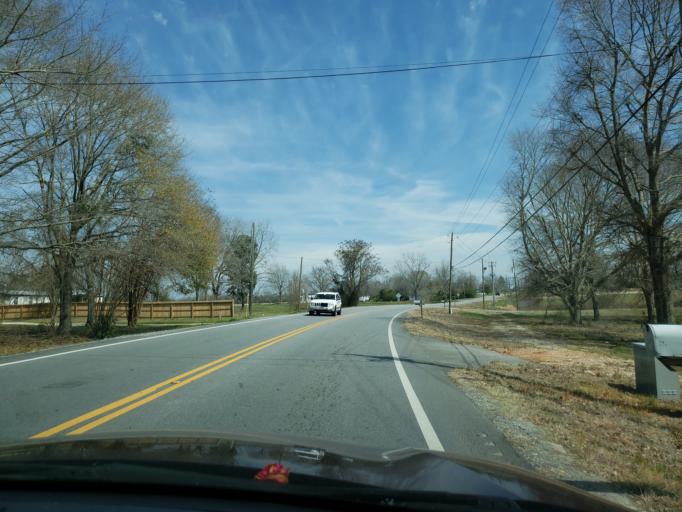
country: US
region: Alabama
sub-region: Elmore County
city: Tallassee
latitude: 32.5600
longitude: -85.8137
